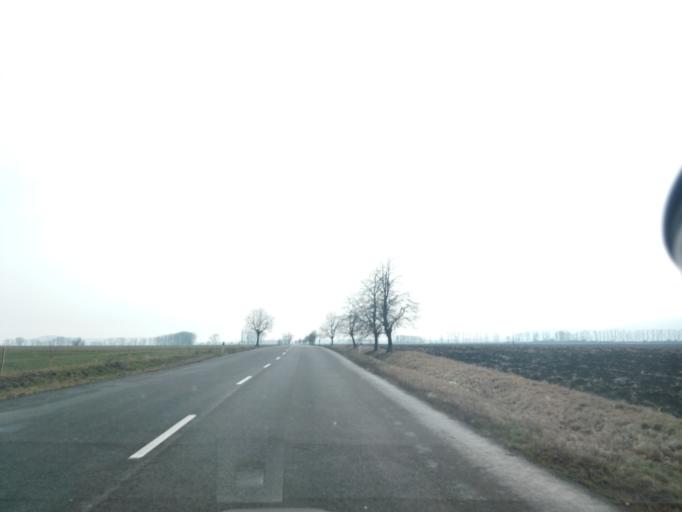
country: SK
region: Kosicky
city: Trebisov
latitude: 48.5549
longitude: 21.6775
